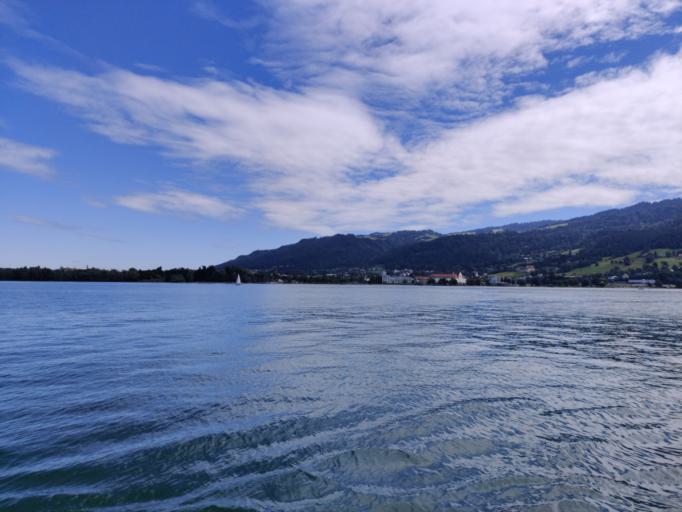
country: AT
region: Vorarlberg
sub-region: Politischer Bezirk Bregenz
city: Lochau
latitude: 47.5218
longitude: 9.7315
